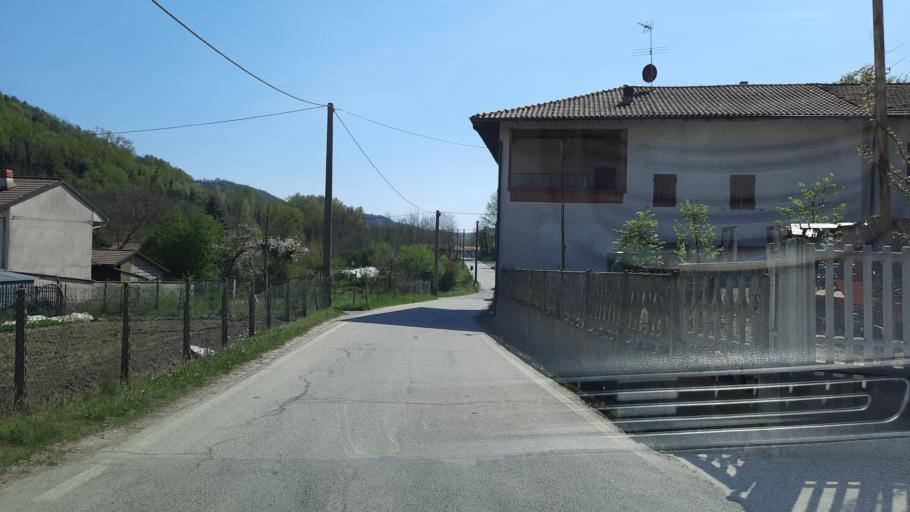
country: IT
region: Piedmont
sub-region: Provincia di Alessandria
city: Moncestino
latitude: 45.1585
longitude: 8.1314
